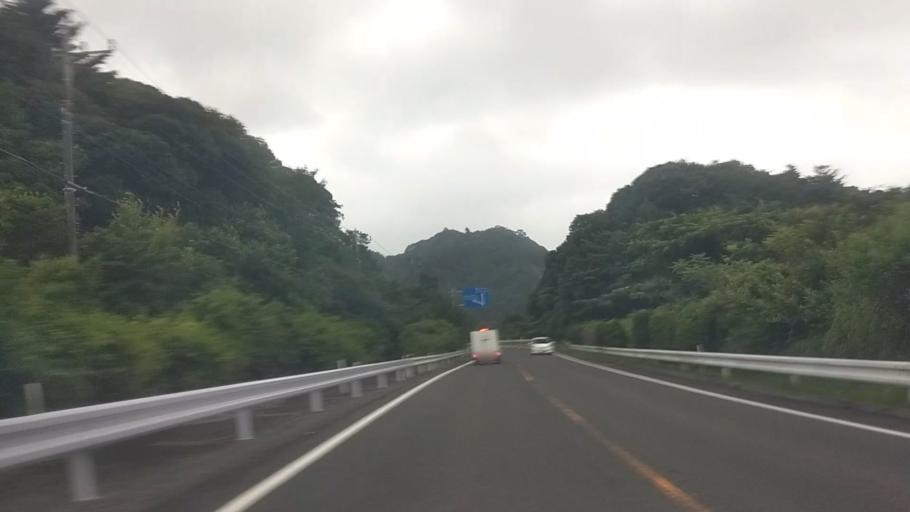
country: JP
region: Chiba
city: Kawaguchi
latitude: 35.1596
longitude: 140.0656
